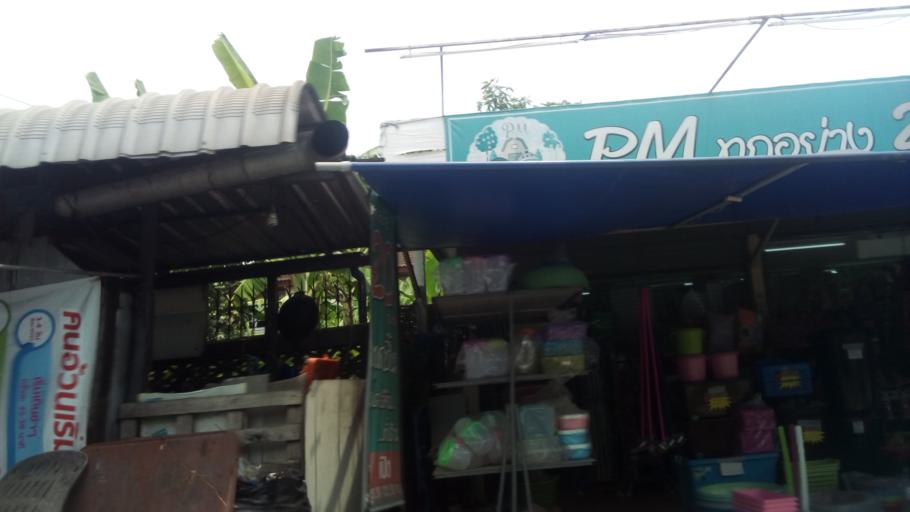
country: TH
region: Nakhon Pathom
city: Salaya
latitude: 13.7692
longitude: 100.2860
